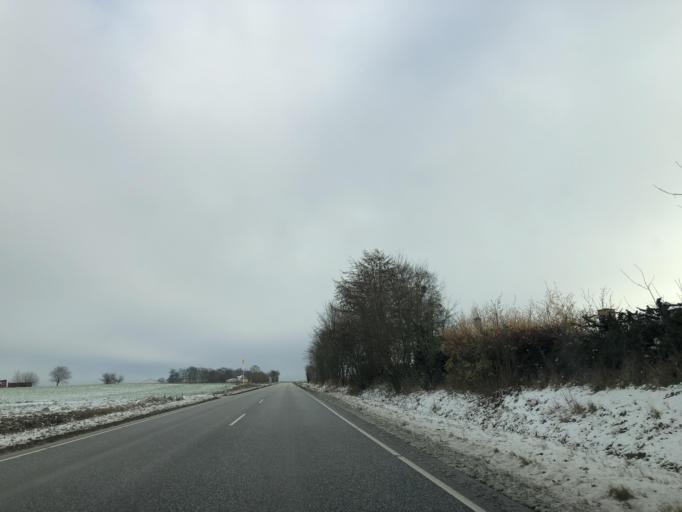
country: DK
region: Central Jutland
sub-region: Horsens Kommune
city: Braedstrup
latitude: 55.8928
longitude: 9.6565
